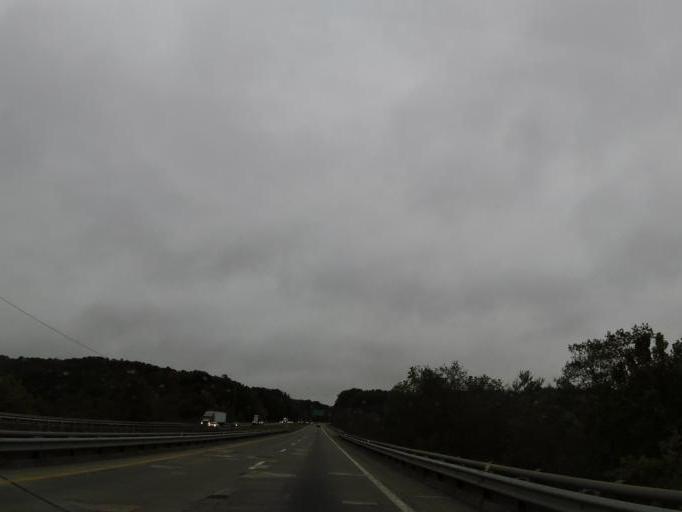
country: US
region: Virginia
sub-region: Wythe County
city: Wytheville
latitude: 36.9827
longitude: -81.0726
